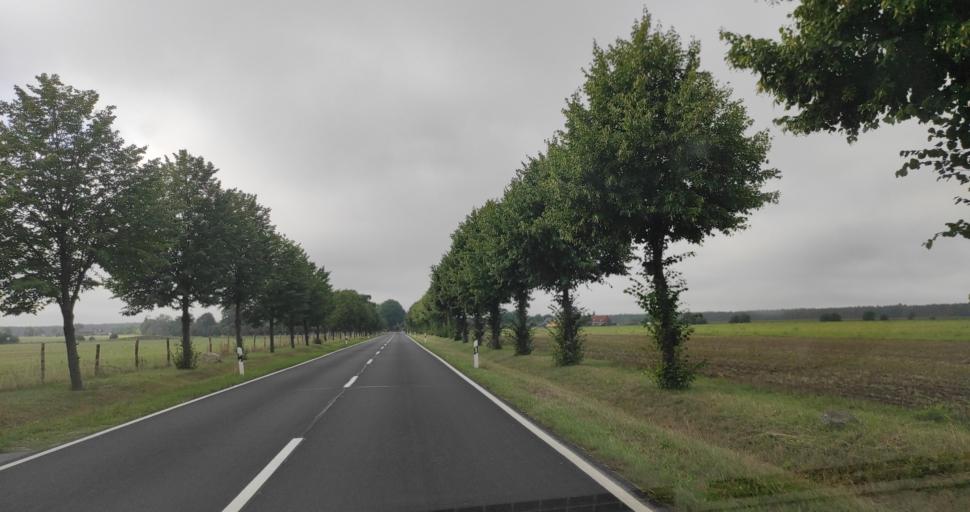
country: DE
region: Brandenburg
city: Heinersbruck
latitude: 51.7335
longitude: 14.5418
